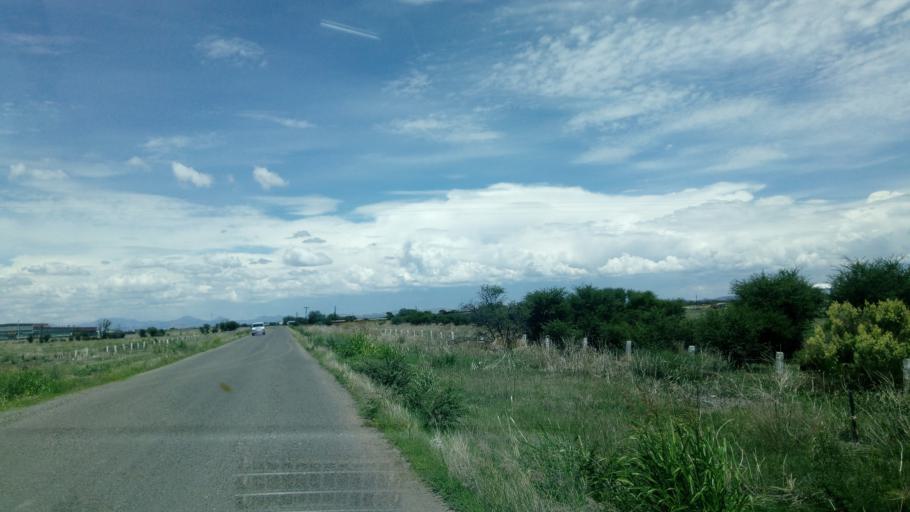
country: MX
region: Durango
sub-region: Durango
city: Jose Refugio Salcido
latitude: 24.1656
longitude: -104.5010
